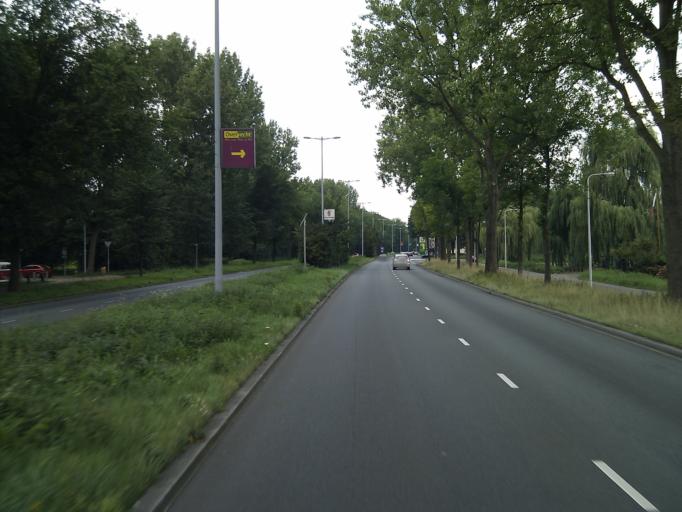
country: NL
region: Utrecht
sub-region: Gemeente Utrecht
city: Utrecht
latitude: 52.1191
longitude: 5.1256
